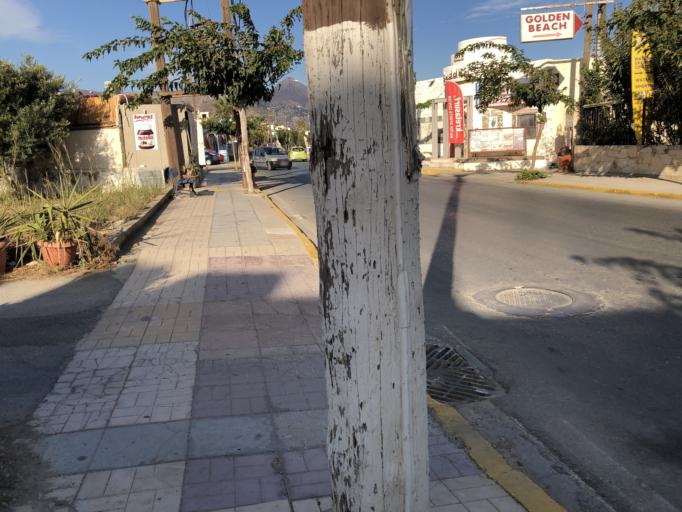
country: GR
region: Crete
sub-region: Nomos Irakleiou
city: Gazi
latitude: 35.3359
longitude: 25.0766
